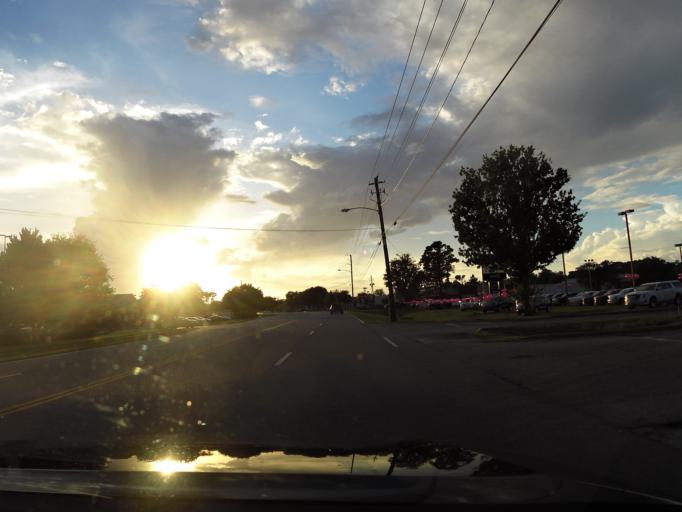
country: US
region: Georgia
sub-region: Glynn County
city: Country Club Estates
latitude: 31.2150
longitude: -81.4818
